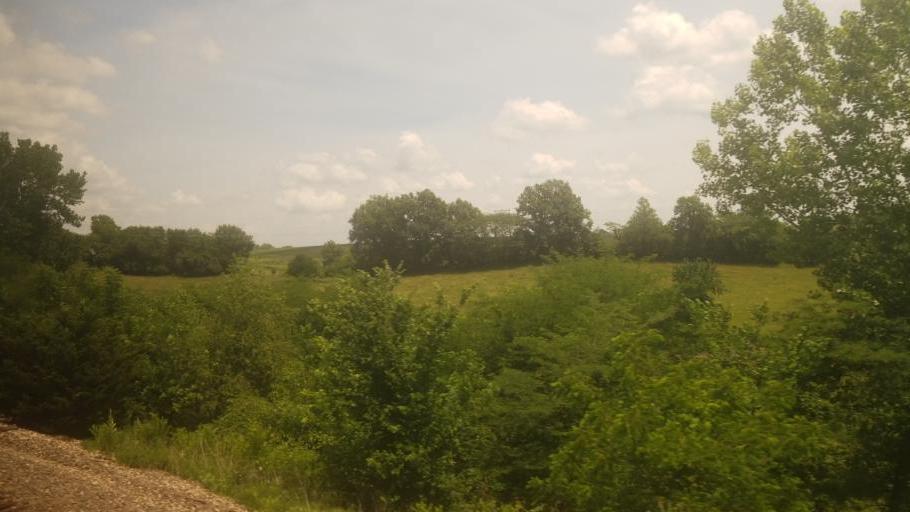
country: US
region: Missouri
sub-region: Macon County
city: La Plata
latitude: 40.0466
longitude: -92.4705
